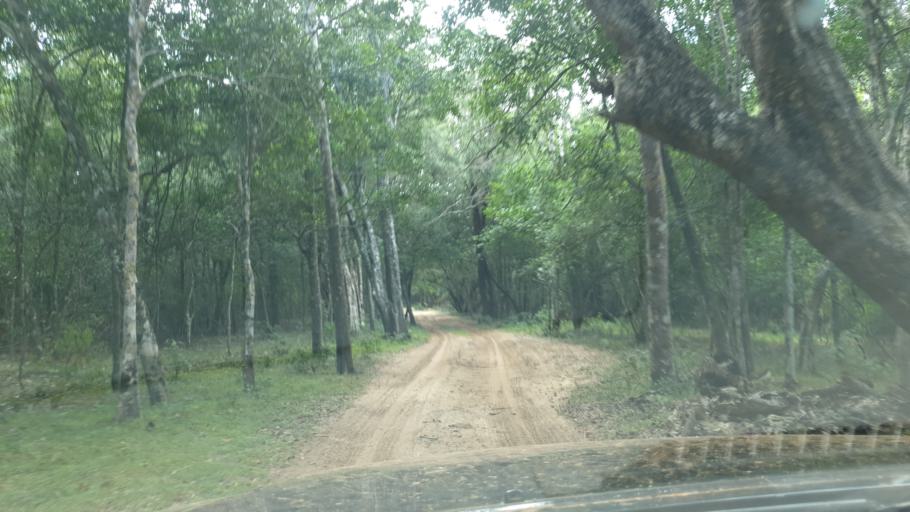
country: LK
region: North Central
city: Anuradhapura
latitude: 8.4202
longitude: 80.0126
